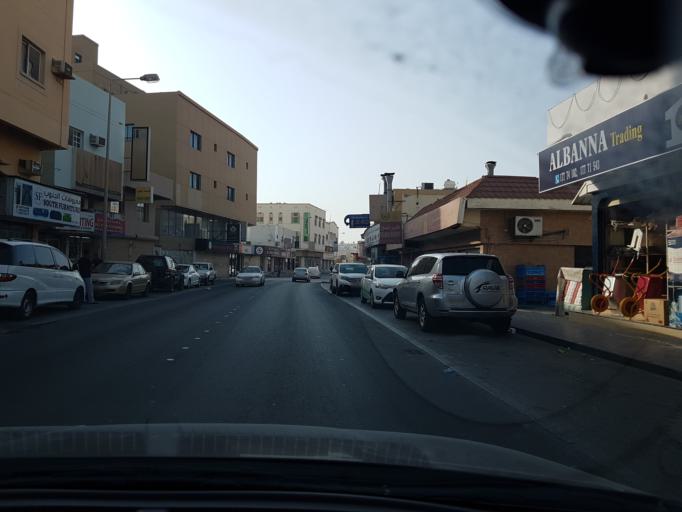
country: BH
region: Northern
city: Ar Rifa'
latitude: 26.1182
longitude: 50.5691
